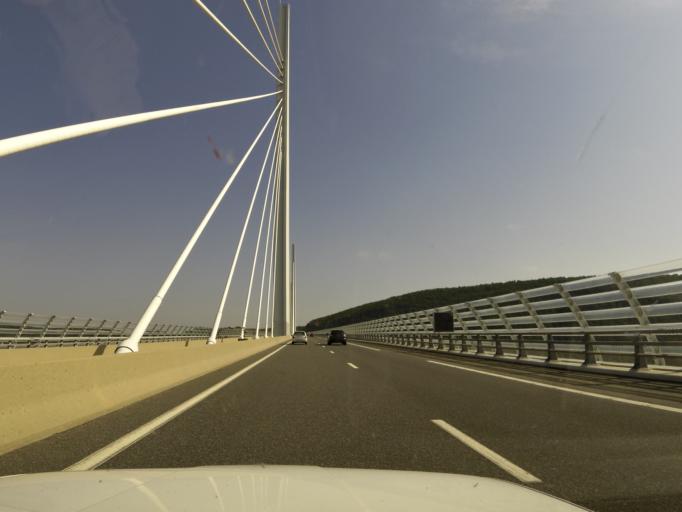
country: FR
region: Midi-Pyrenees
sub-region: Departement de l'Aveyron
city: Creissels
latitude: 44.0811
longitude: 3.0221
